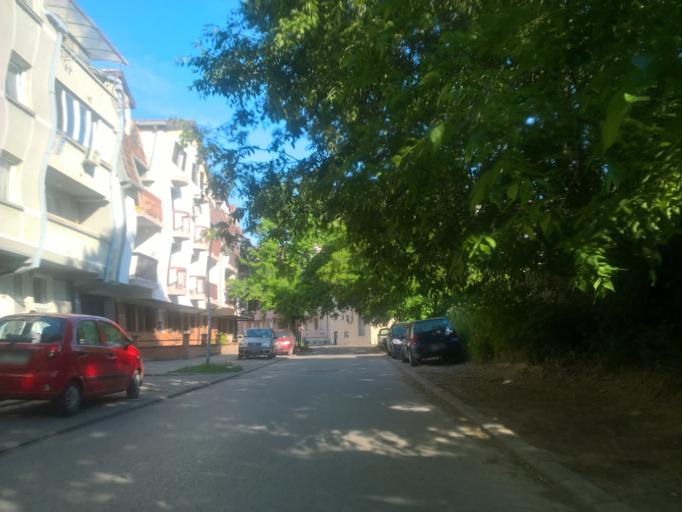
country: RS
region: Autonomna Pokrajina Vojvodina
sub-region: Juznobacki Okrug
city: Novi Sad
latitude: 45.2429
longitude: 19.8277
